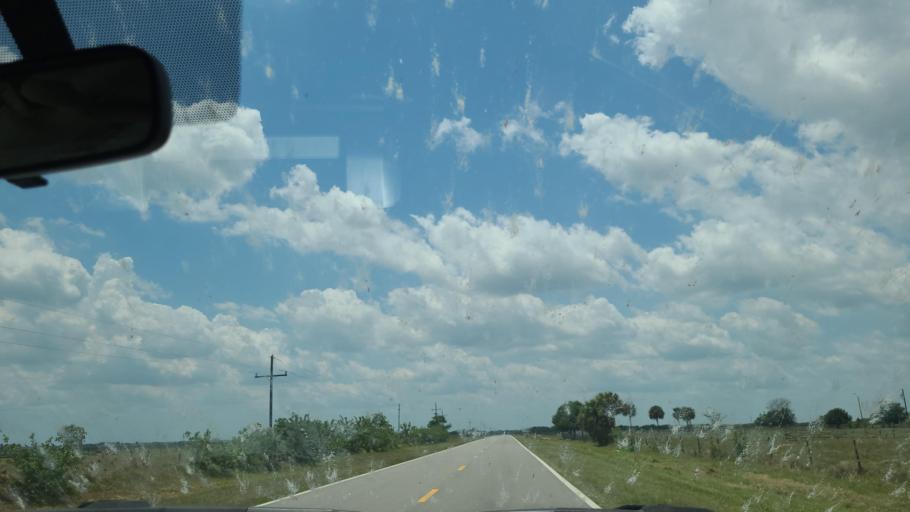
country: US
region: Florida
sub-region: Glades County
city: Buckhead Ridge
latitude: 27.2601
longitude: -81.0539
